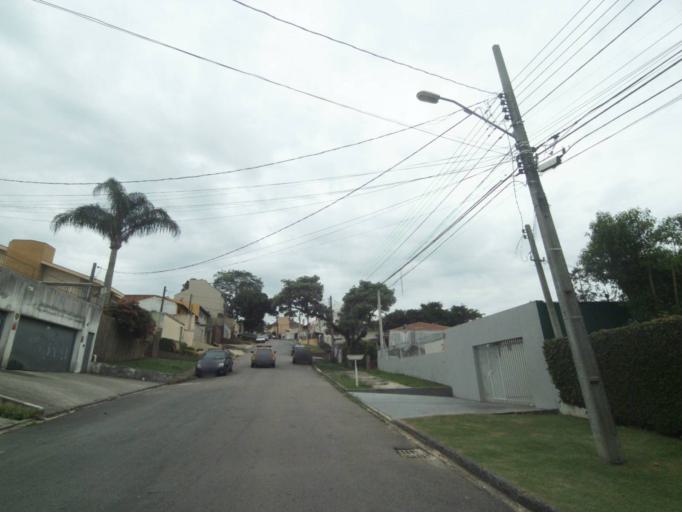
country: BR
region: Parana
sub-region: Curitiba
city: Curitiba
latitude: -25.3961
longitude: -49.2922
